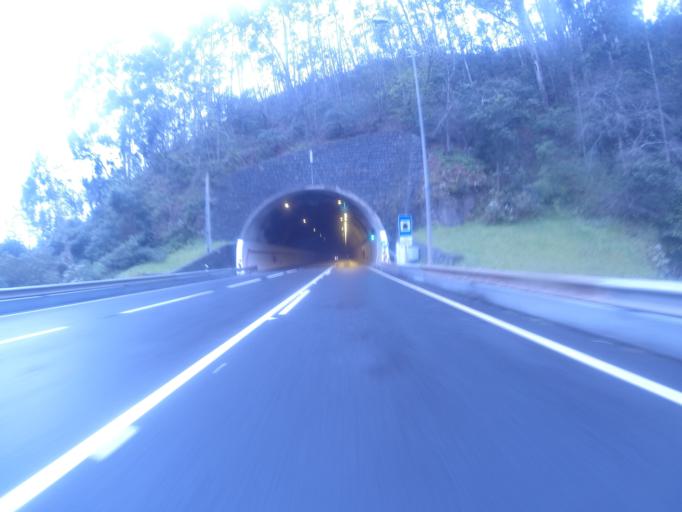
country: PT
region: Madeira
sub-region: Santa Cruz
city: Camacha
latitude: 32.6693
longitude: -16.8508
